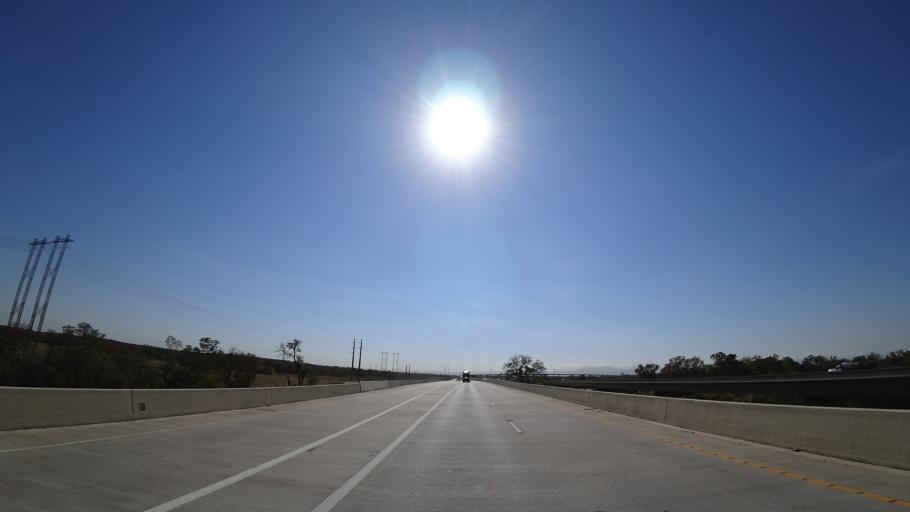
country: US
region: Texas
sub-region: Travis County
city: Hornsby Bend
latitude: 30.2105
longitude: -97.6222
